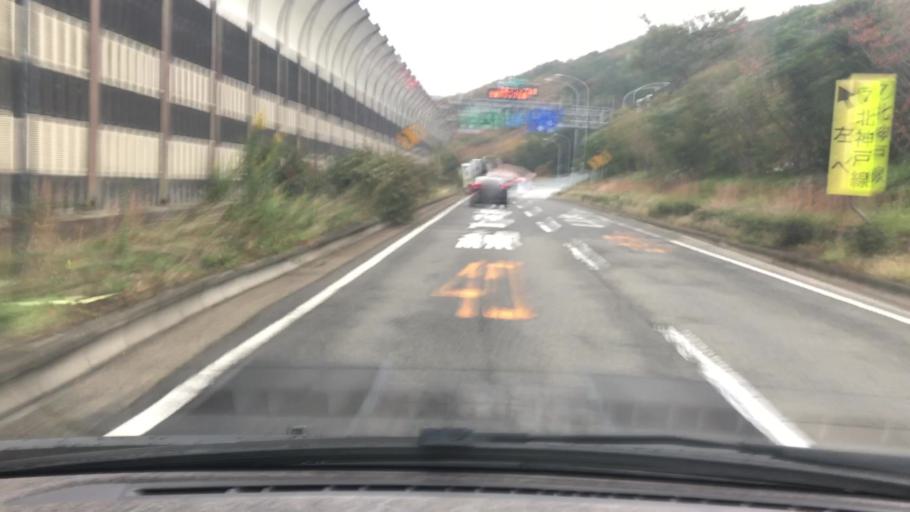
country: JP
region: Hyogo
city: Kobe
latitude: 34.7574
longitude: 135.1604
